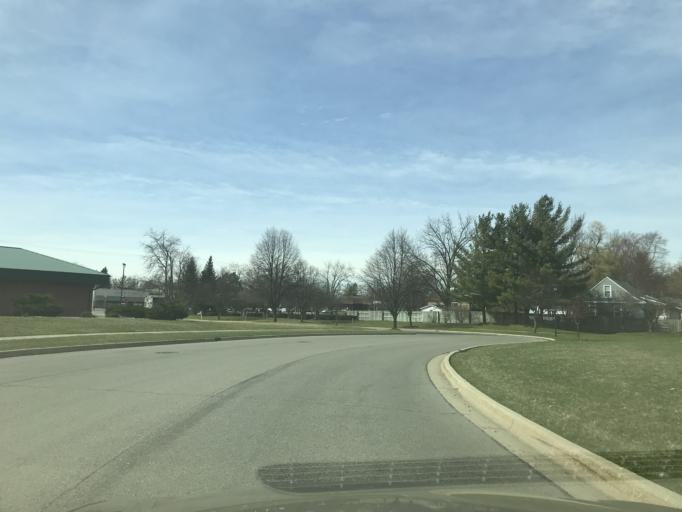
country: US
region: Michigan
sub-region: Eaton County
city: Grand Ledge
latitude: 42.7420
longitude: -84.7381
